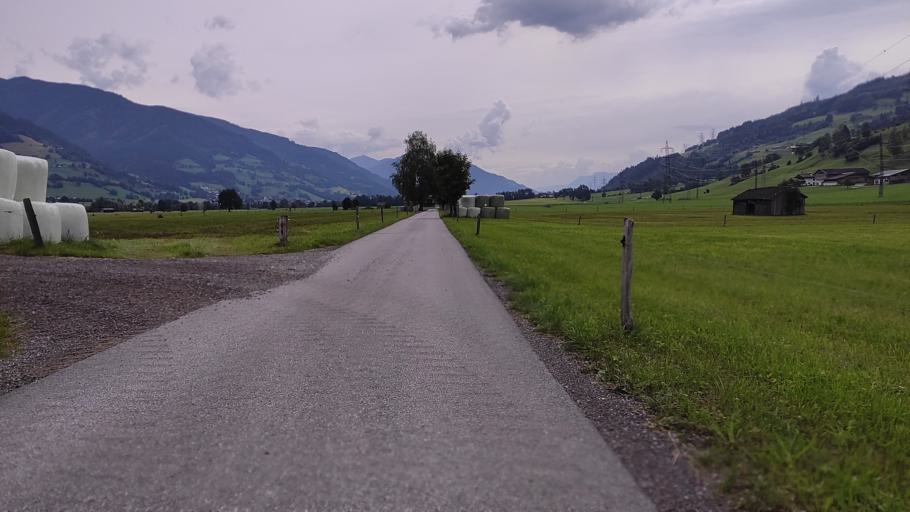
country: AT
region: Salzburg
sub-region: Politischer Bezirk Zell am See
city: Niedernsill
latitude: 47.2771
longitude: 12.6753
